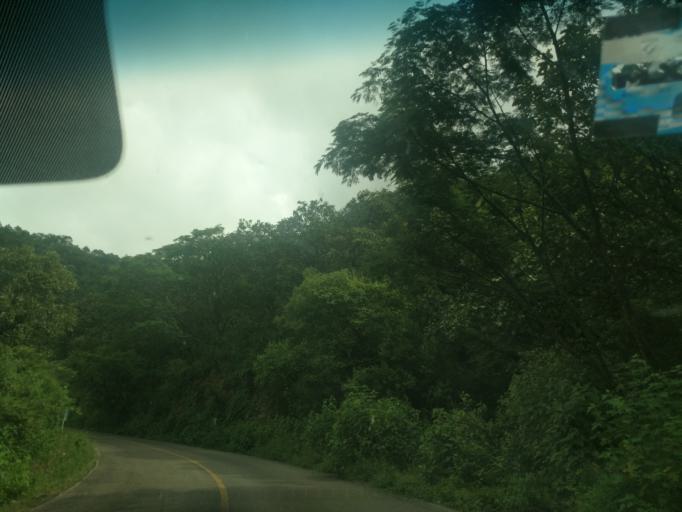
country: MX
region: Jalisco
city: El Salto
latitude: 20.3662
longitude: -104.5880
